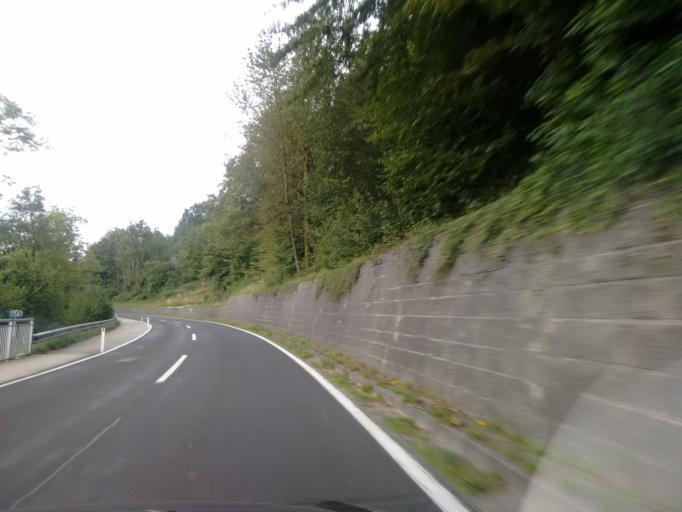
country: AT
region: Upper Austria
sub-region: Politischer Bezirk Vocklabruck
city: Steinbach am Attersee
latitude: 47.8557
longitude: 13.5589
